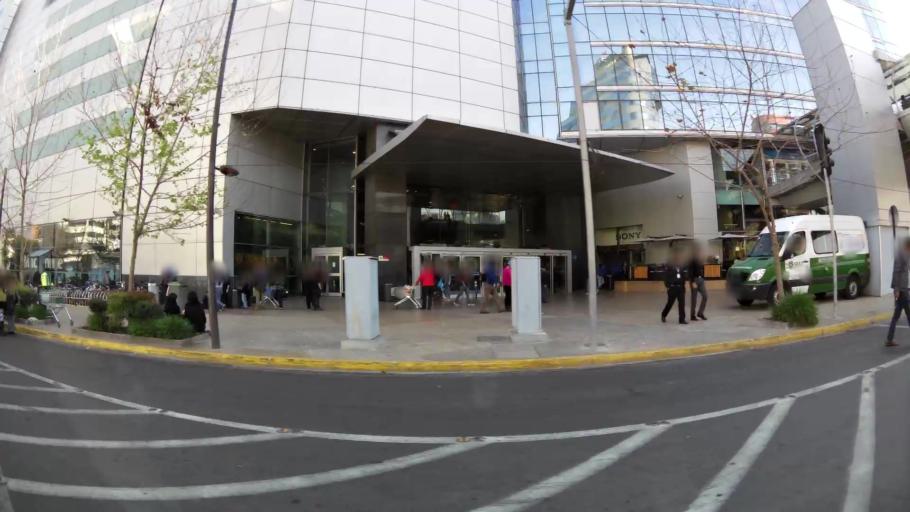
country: CL
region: Santiago Metropolitan
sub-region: Provincia de Santiago
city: Villa Presidente Frei, Nunoa, Santiago, Chile
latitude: -33.4178
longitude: -70.6052
